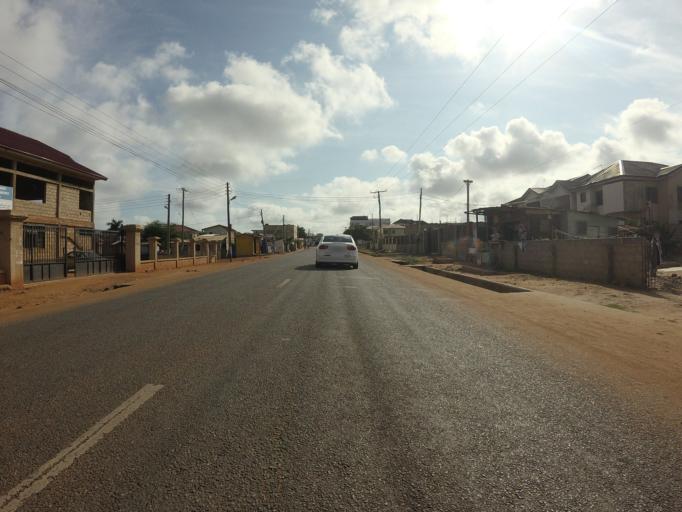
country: GH
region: Greater Accra
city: Teshi Old Town
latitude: 5.5865
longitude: -0.1405
